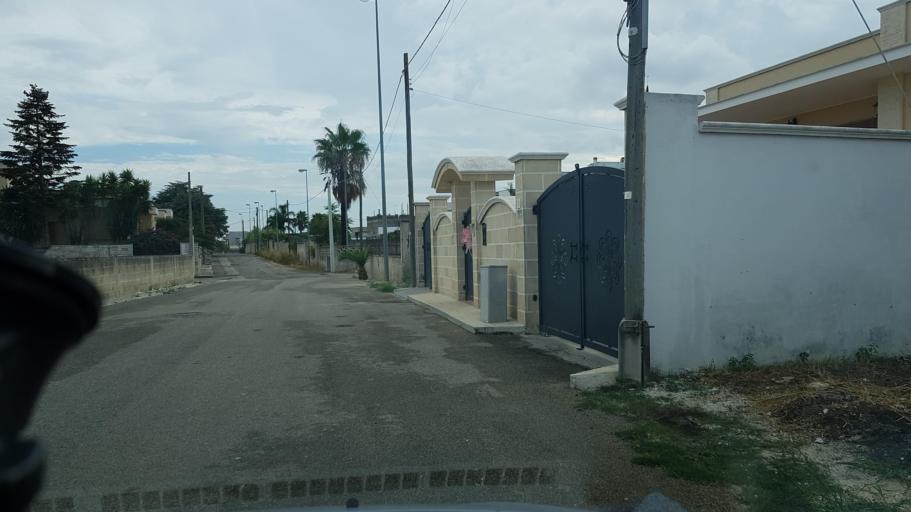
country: IT
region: Apulia
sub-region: Provincia di Brindisi
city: Torre Santa Susanna
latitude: 40.4734
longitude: 17.7418
